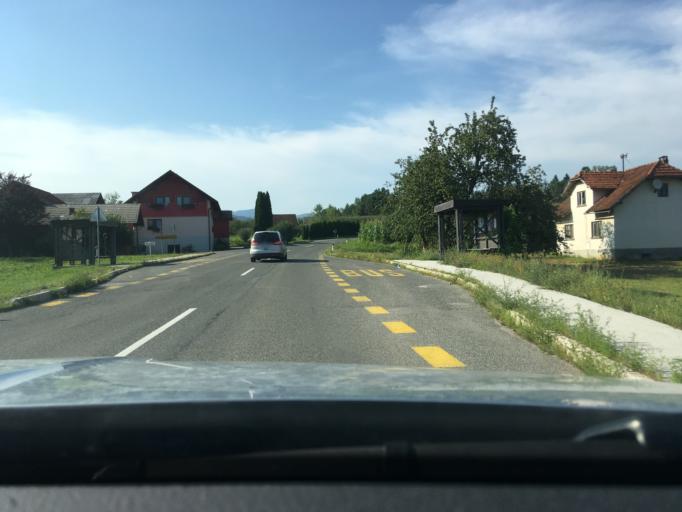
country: SI
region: Crnomelj
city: Crnomelj
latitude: 45.5424
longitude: 15.1593
